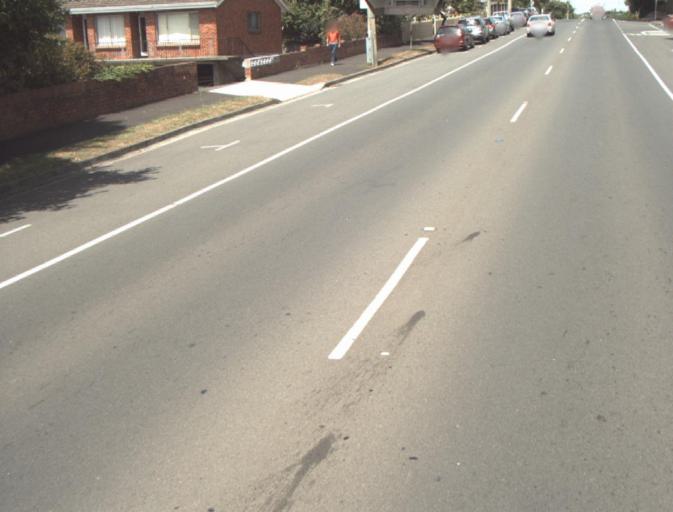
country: AU
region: Tasmania
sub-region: Launceston
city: East Launceston
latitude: -41.4368
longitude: 147.1573
